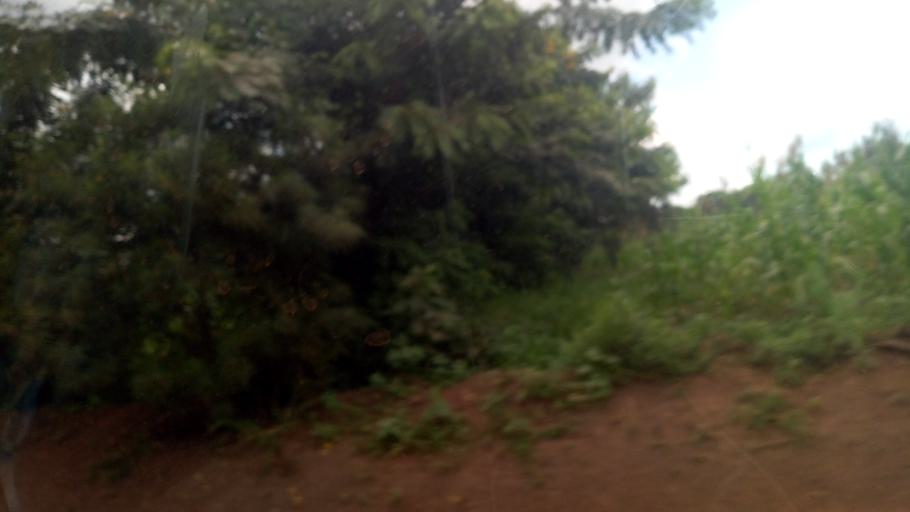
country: UG
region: Western Region
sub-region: Kiryandongo District
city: Kiryandongo
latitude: 1.9293
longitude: 32.1324
